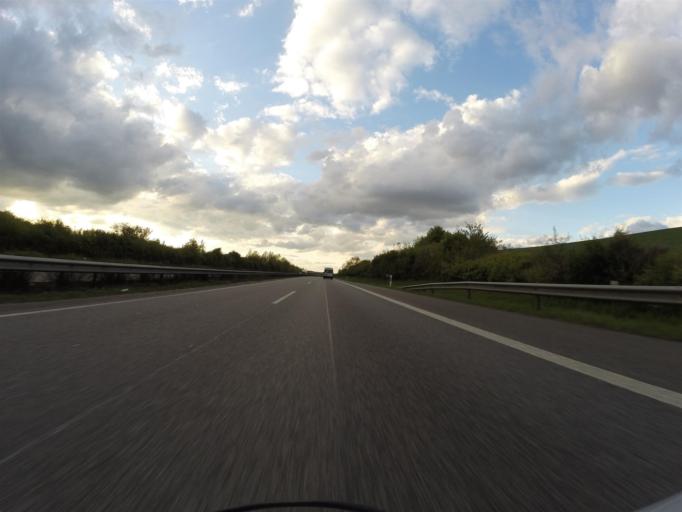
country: DE
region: Rheinland-Pfalz
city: Kirchheimbolanden
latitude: 49.6509
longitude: 8.0295
